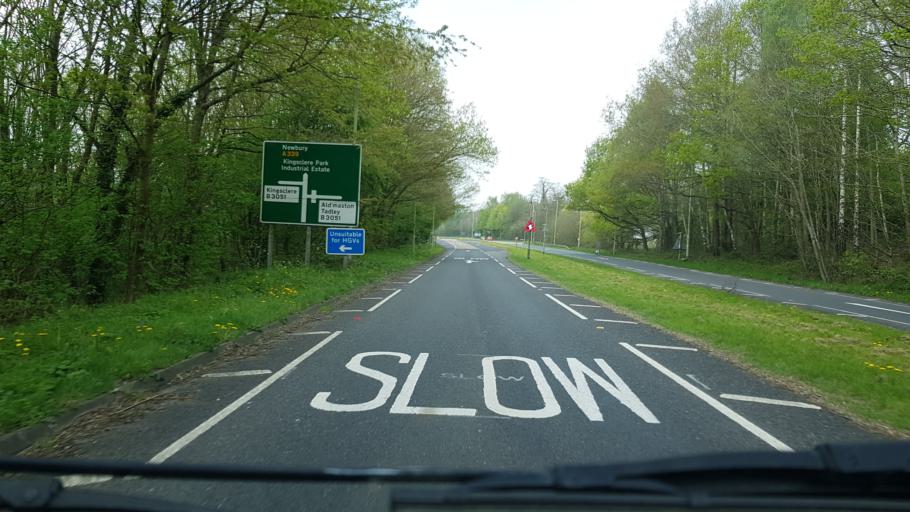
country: GB
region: England
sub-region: Hampshire
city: Kingsclere
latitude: 51.3264
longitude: -1.2362
